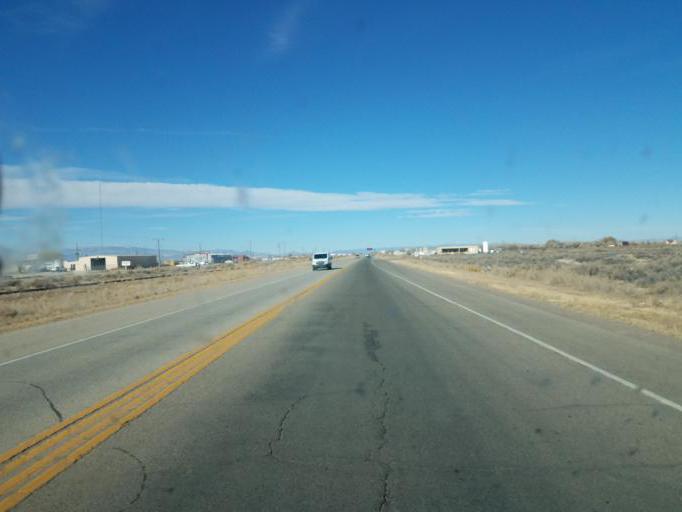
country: US
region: Colorado
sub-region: Alamosa County
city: Alamosa
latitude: 37.4841
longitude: -105.9157
